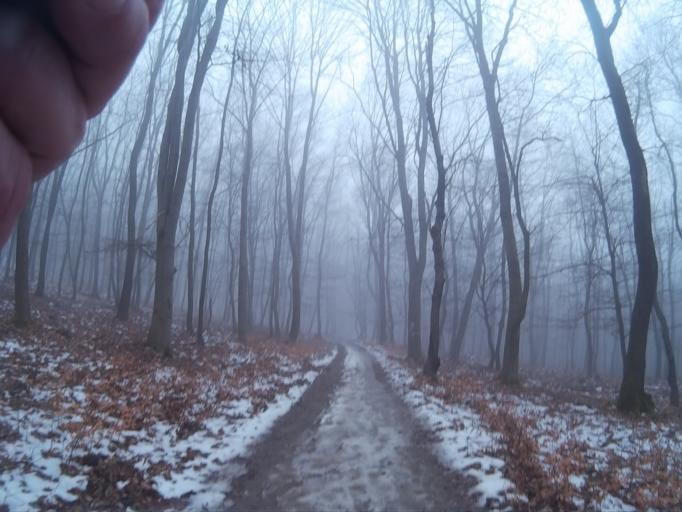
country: HU
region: Komarom-Esztergom
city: Tardos
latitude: 47.6839
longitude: 18.4746
